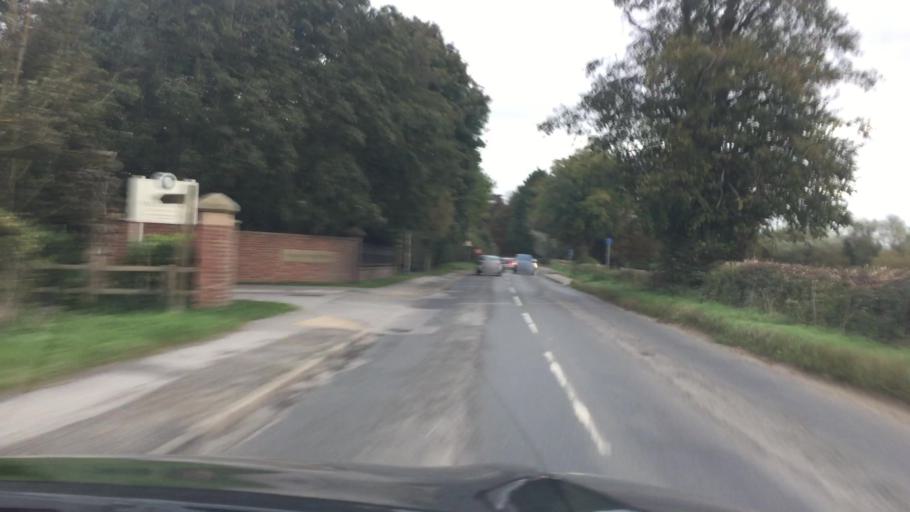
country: GB
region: England
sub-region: East Riding of Yorkshire
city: Pocklington
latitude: 53.9238
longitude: -0.7873
